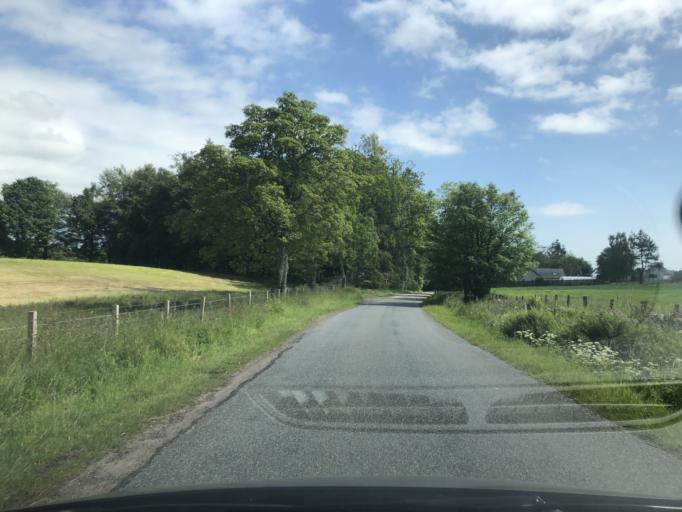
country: GB
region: Scotland
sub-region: Angus
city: Kirriemuir
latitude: 56.7313
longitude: -3.0066
